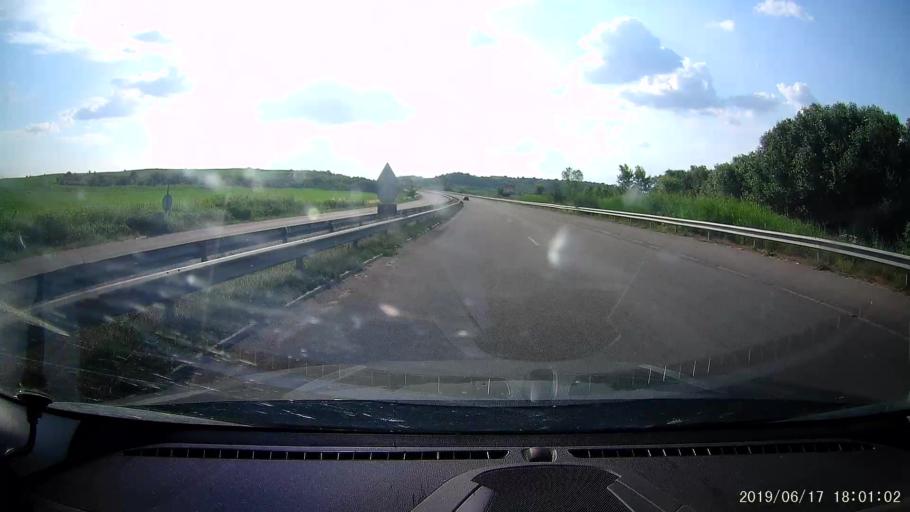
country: BG
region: Khaskovo
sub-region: Obshtina Svilengrad
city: Svilengrad
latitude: 41.7432
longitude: 26.2662
